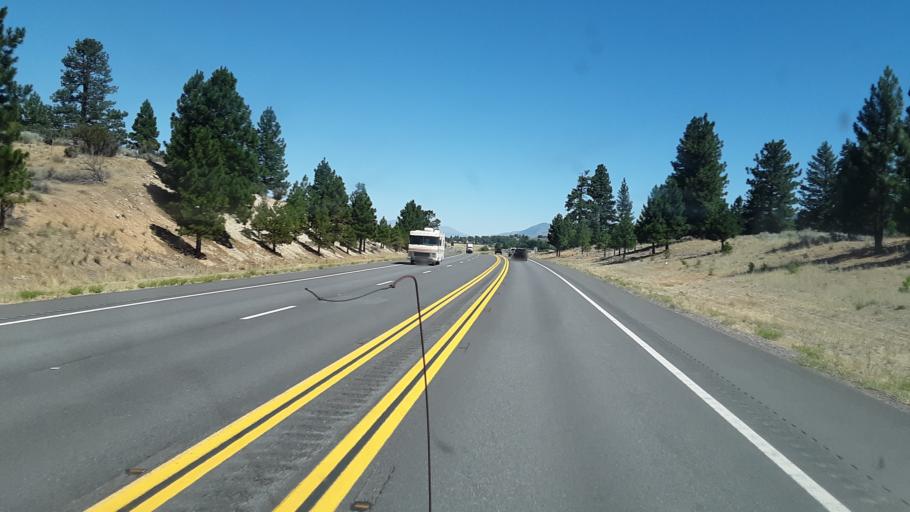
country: US
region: California
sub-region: Lassen County
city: Janesville
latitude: 40.3055
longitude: -120.5280
